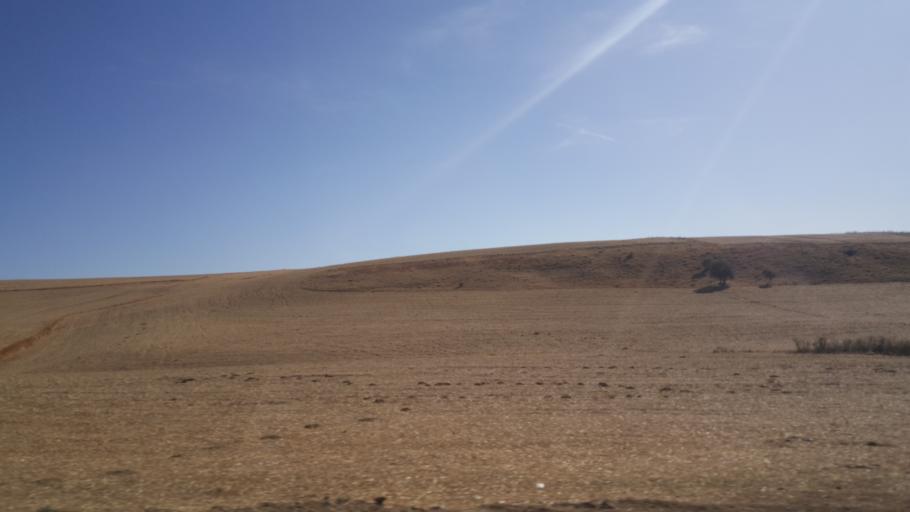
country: TR
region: Ankara
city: Yenice
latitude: 39.2888
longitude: 32.6219
